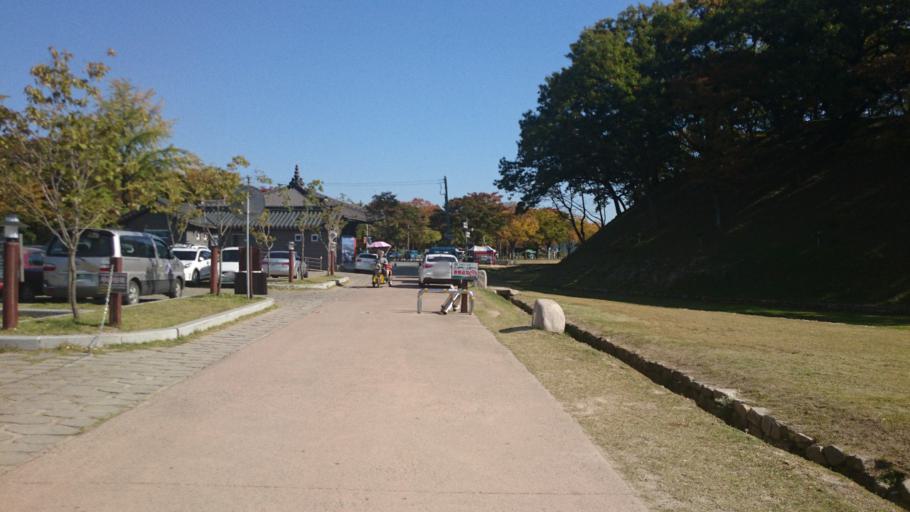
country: KR
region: Gyeongsangbuk-do
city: Kyonju
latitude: 35.8339
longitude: 129.2240
